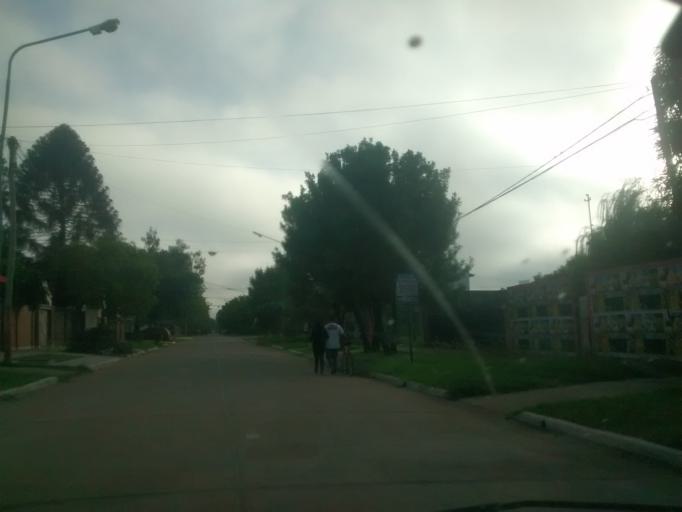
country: AR
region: Chaco
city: Resistencia
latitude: -27.4622
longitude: -58.9971
